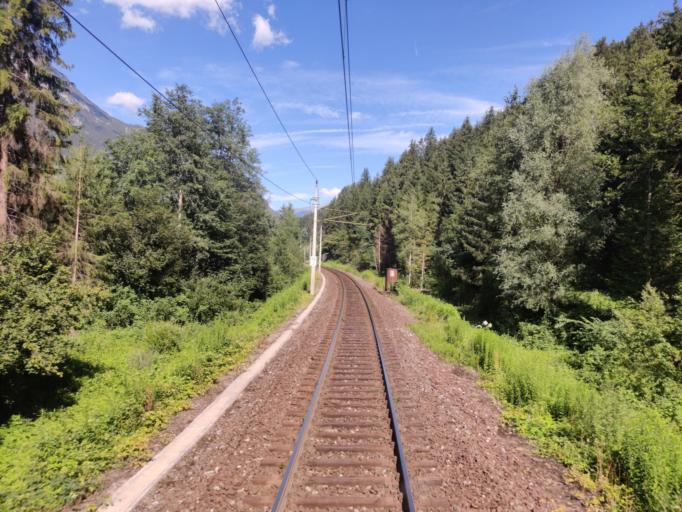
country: AT
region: Tyrol
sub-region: Politischer Bezirk Imst
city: Karrosten
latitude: 47.2155
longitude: 10.7429
